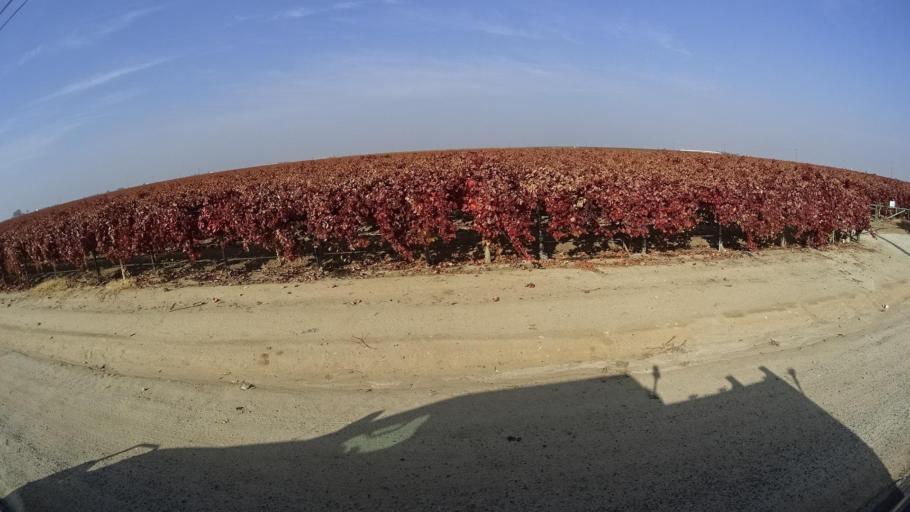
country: US
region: California
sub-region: Tulare County
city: Richgrove
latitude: 35.7760
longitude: -119.1720
